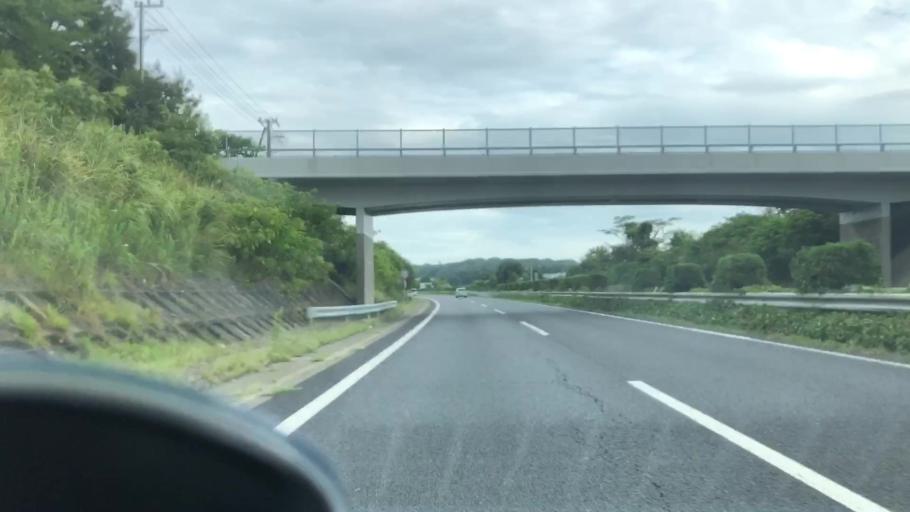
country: JP
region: Hyogo
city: Yashiro
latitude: 34.9221
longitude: 134.9921
